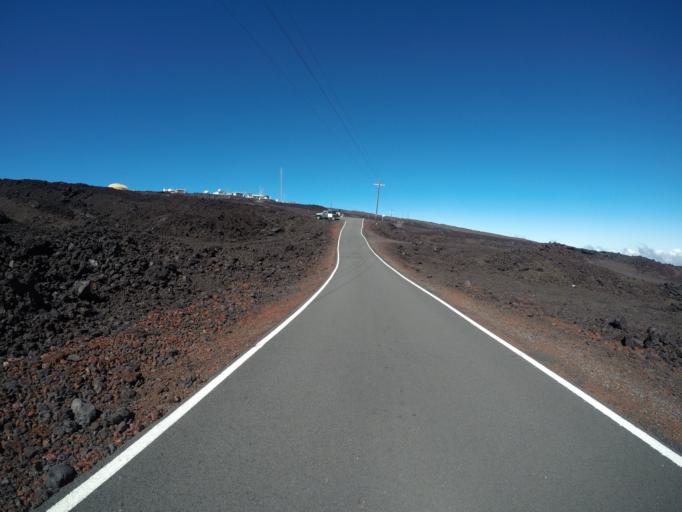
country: US
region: Hawaii
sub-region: Hawaii County
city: Honaunau-Napoopoo
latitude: 19.5406
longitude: -155.5772
